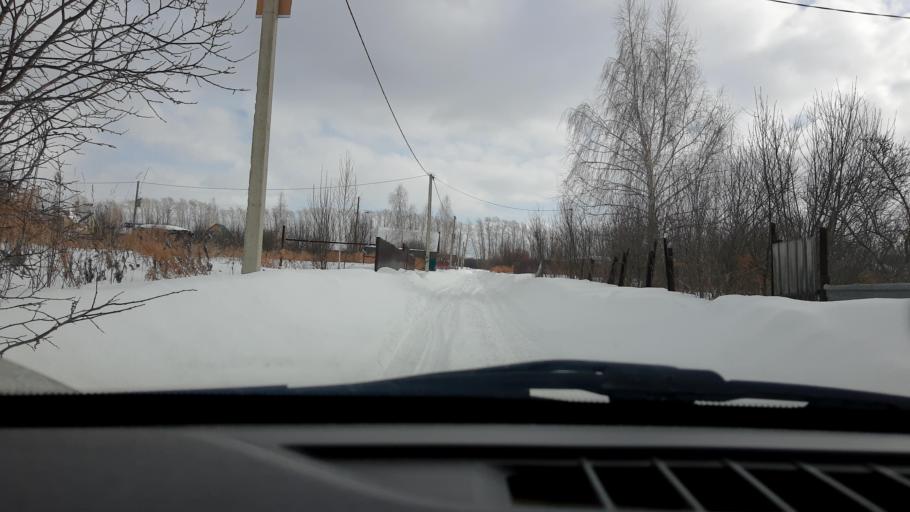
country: RU
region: Bashkortostan
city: Iglino
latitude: 54.7310
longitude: 56.2306
